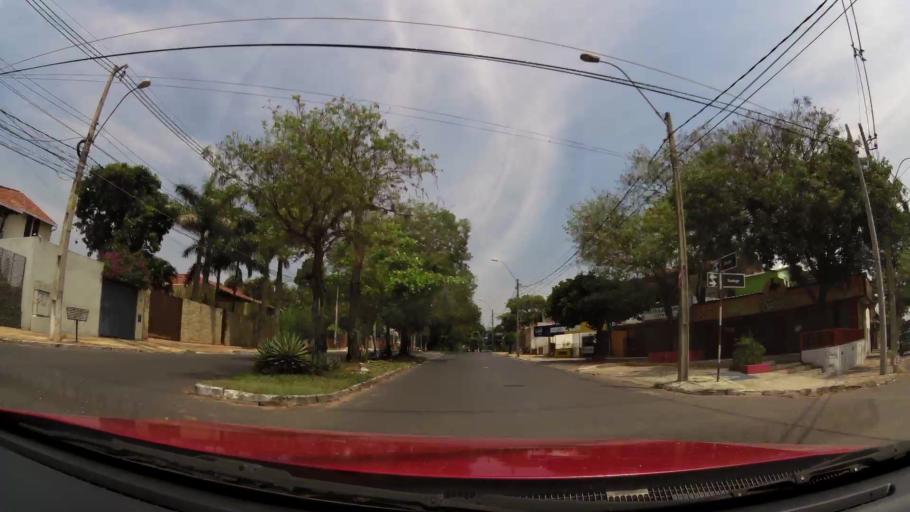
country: PY
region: Asuncion
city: Asuncion
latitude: -25.2727
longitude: -57.5986
